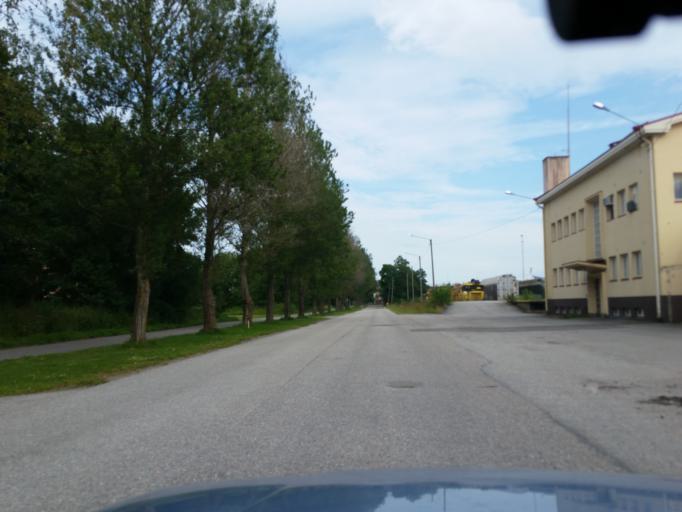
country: FI
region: Uusimaa
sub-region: Raaseporin
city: Hanko
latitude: 59.8269
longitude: 22.9588
